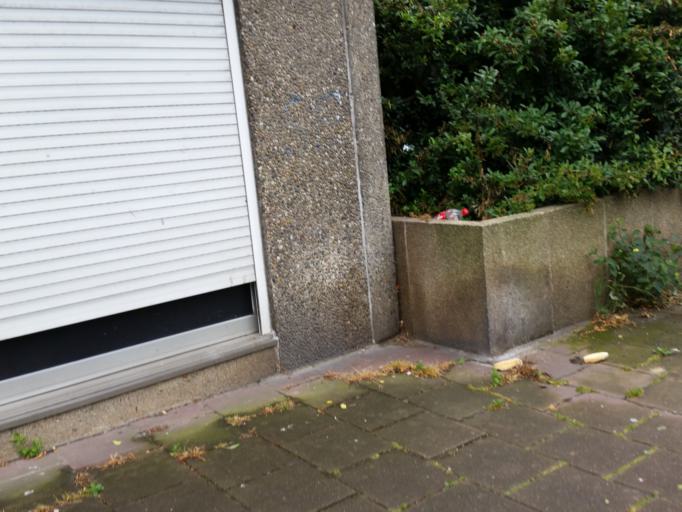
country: BE
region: Brussels Capital
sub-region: Bruxelles-Capitale
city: Brussels
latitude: 50.8638
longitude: 4.3578
